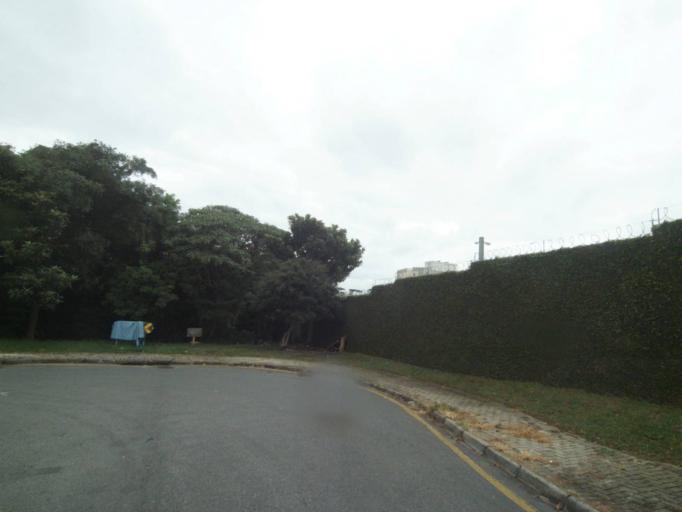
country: BR
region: Parana
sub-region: Curitiba
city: Curitiba
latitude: -25.4621
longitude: -49.3388
